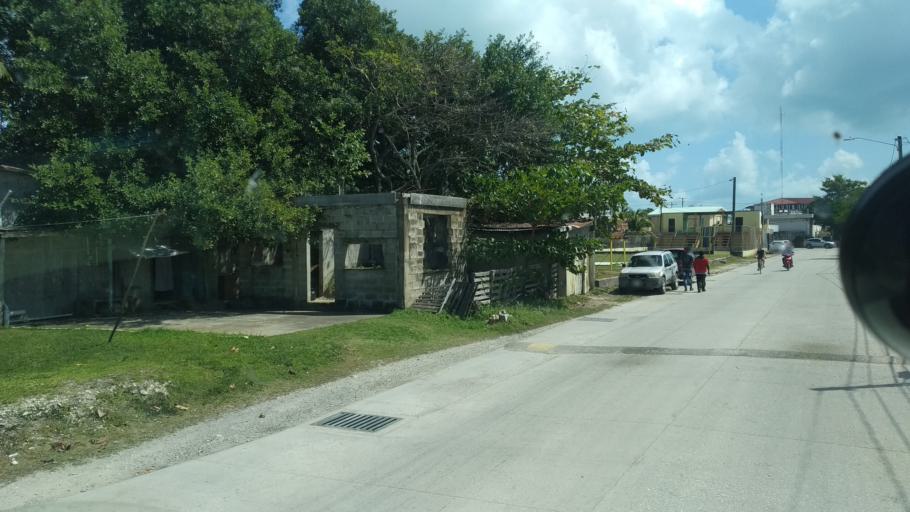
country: BZ
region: Belize
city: Belize City
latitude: 17.5035
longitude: -88.1903
